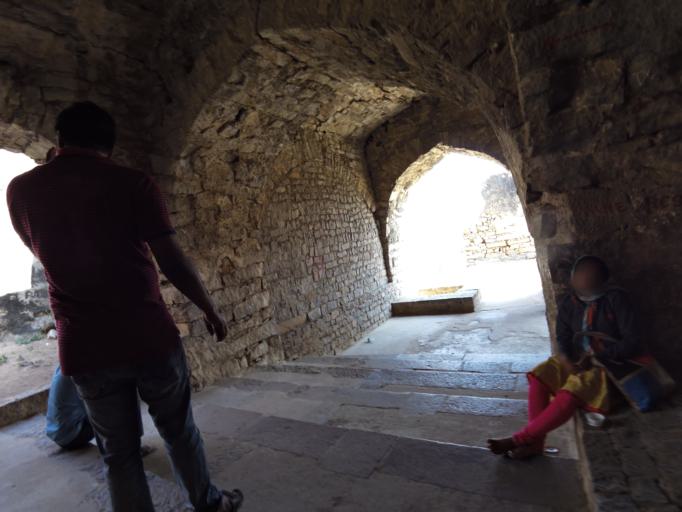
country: IN
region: Telangana
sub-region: Hyderabad
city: Hyderabad
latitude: 17.3822
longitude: 78.4005
